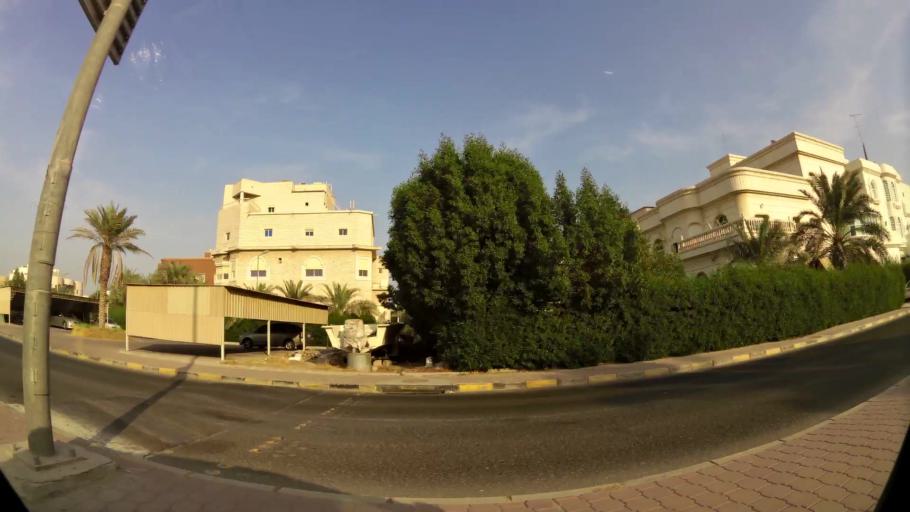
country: KW
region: Mubarak al Kabir
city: Sabah as Salim
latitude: 29.2400
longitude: 48.0773
